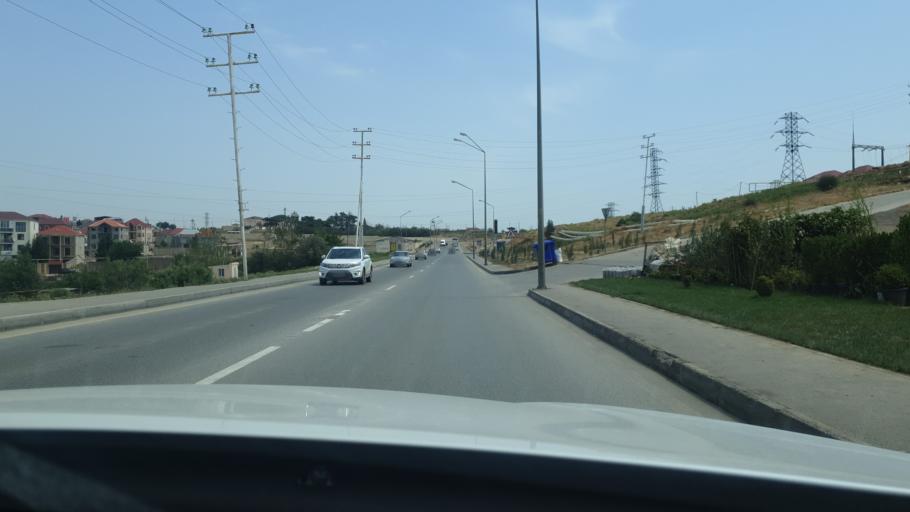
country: AZ
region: Baki
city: Qaracuxur
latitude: 40.3928
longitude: 49.9842
